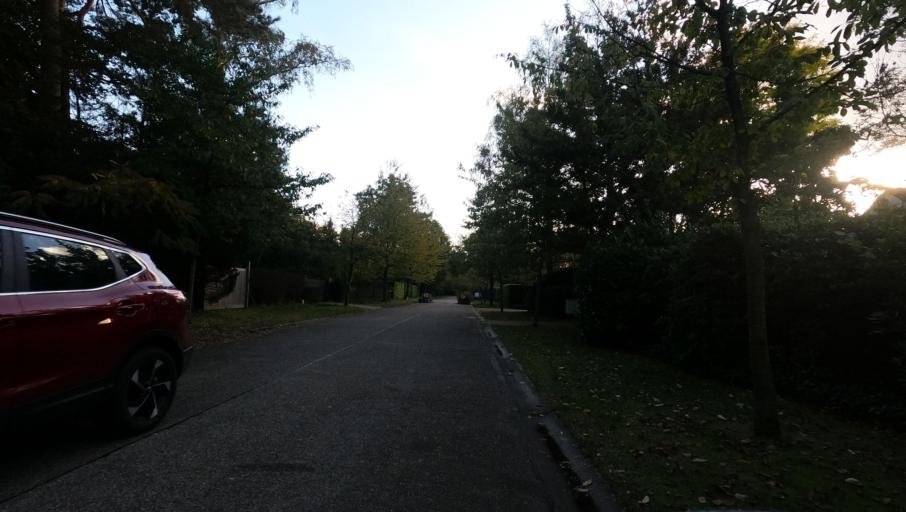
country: BE
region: Flanders
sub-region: Provincie Antwerpen
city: Schilde
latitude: 51.2432
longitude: 4.5686
